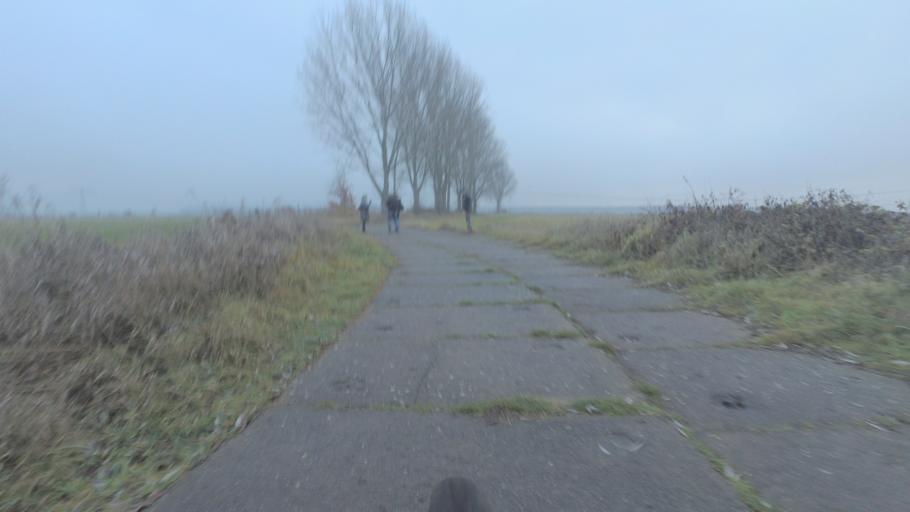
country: DE
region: Brandenburg
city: Grossbeeren
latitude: 52.3286
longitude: 13.3482
